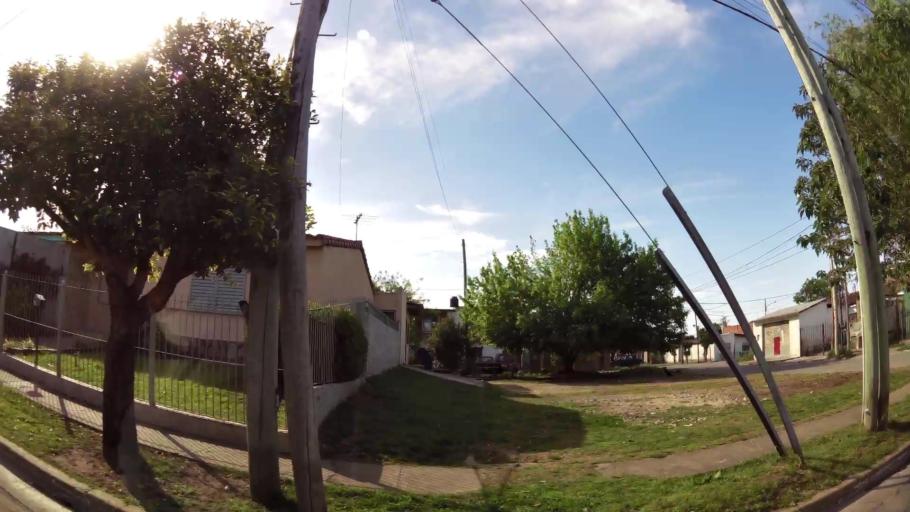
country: AR
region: Buenos Aires
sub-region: Partido de Quilmes
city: Quilmes
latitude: -34.7904
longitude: -58.2306
